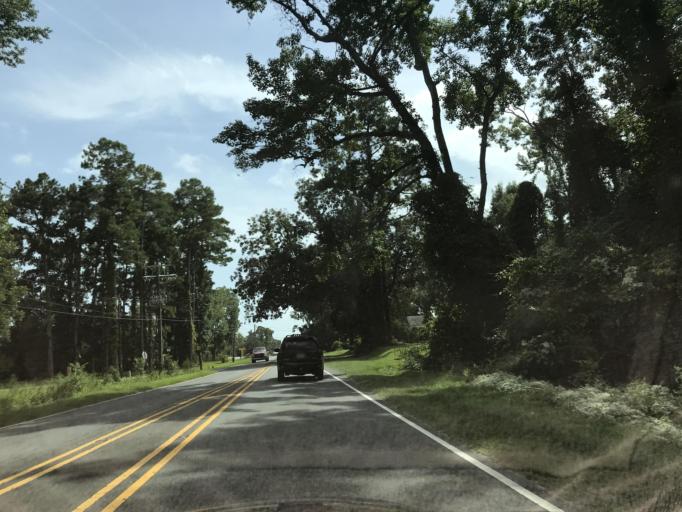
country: US
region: North Carolina
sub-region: New Hanover County
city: Wrightsboro
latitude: 34.3009
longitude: -77.9217
